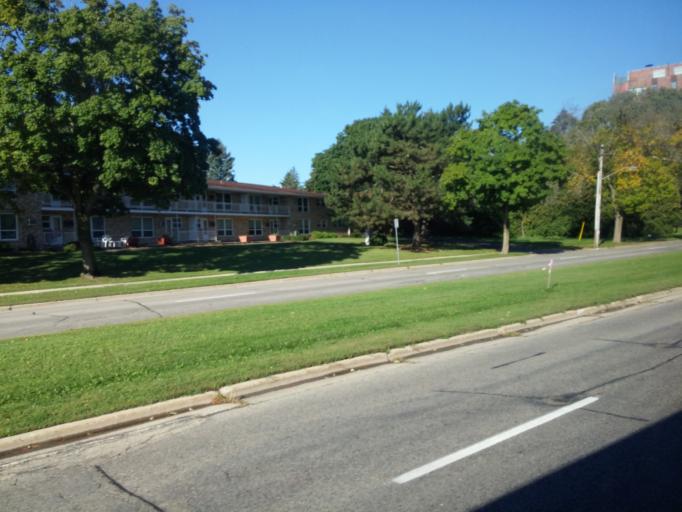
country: US
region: Wisconsin
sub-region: Dane County
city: Shorewood Hills
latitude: 43.0712
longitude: -89.4549
